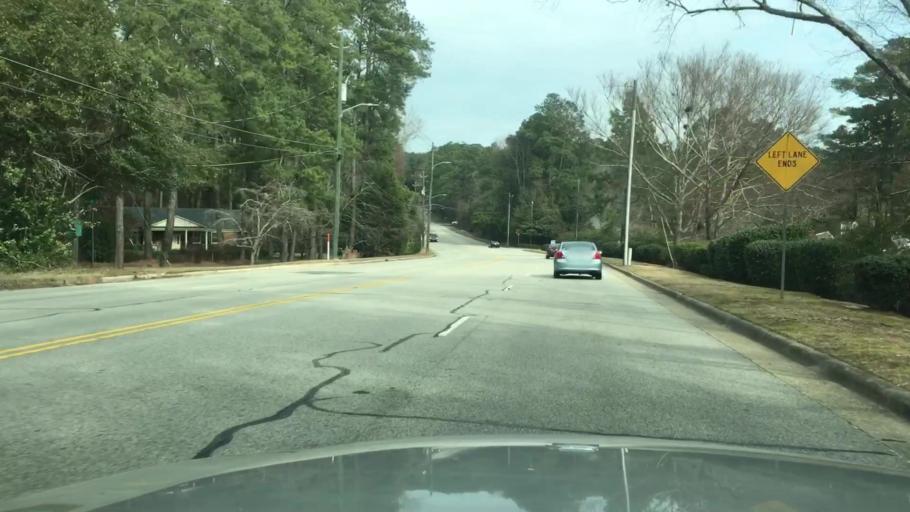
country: US
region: North Carolina
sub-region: Cumberland County
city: Fayetteville
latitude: 35.0481
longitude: -78.9155
